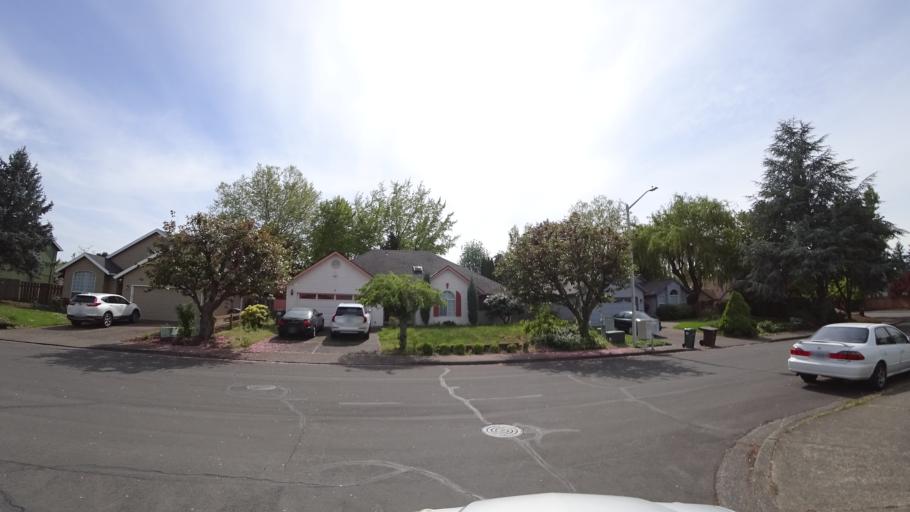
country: US
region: Oregon
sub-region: Washington County
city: Rockcreek
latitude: 45.5358
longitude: -122.9294
